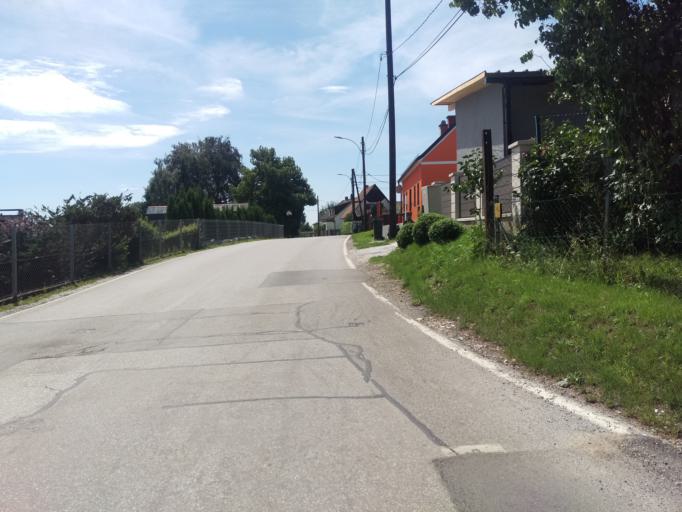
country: AT
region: Styria
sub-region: Politischer Bezirk Graz-Umgebung
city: Feldkirchen bei Graz
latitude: 47.0255
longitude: 15.4413
